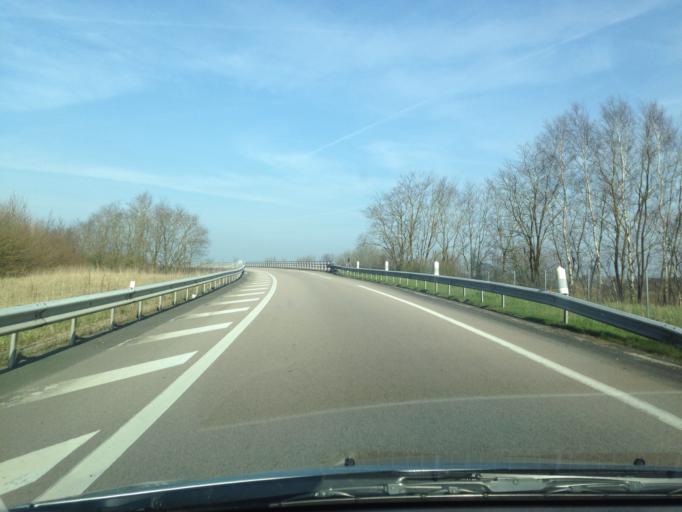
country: FR
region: Haute-Normandie
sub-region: Departement de la Seine-Maritime
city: Saint-Saens
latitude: 49.6497
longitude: 1.2646
